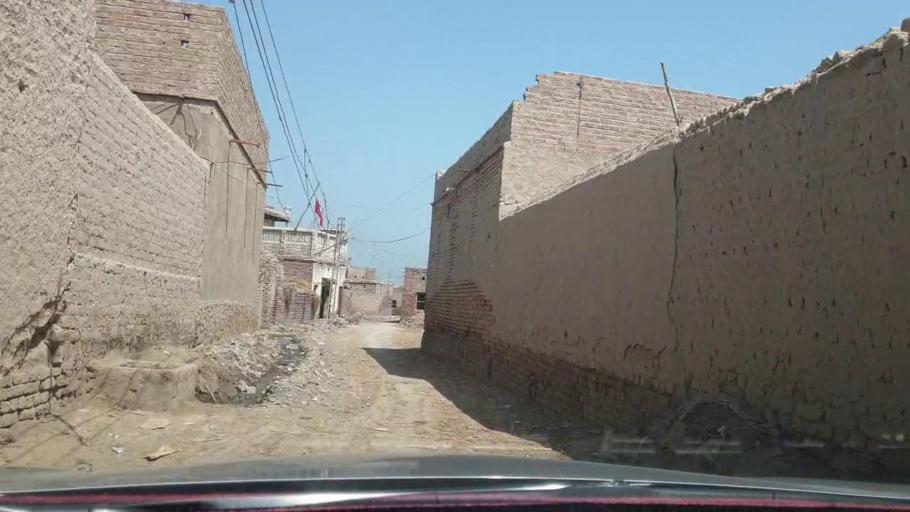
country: PK
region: Sindh
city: Kambar
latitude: 27.5896
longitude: 67.9097
